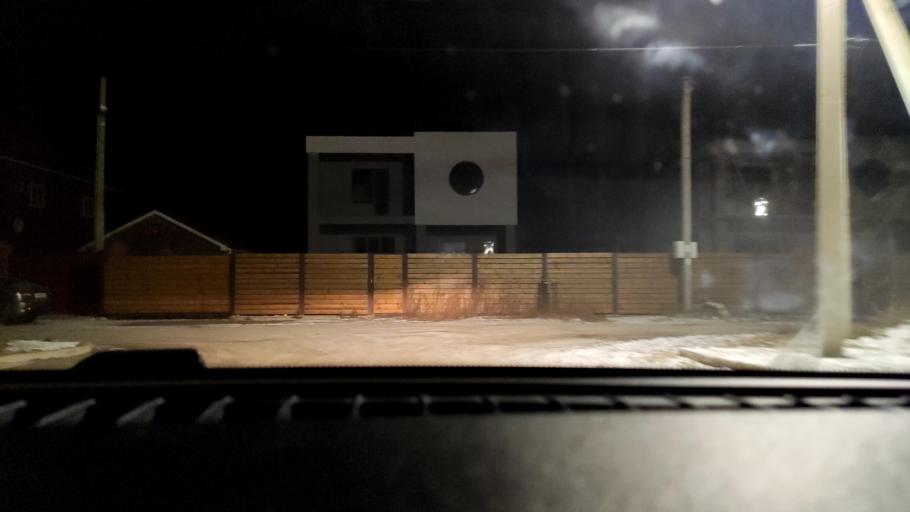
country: RU
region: Samara
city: Samara
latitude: 53.1151
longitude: 50.1770
